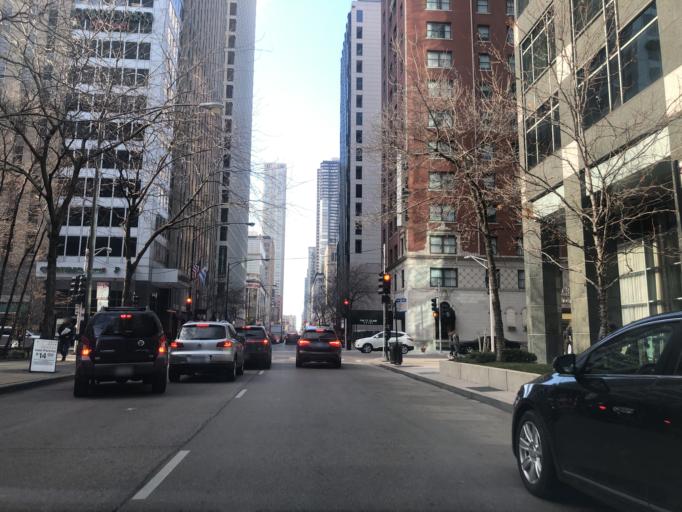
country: US
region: Illinois
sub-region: Cook County
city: Chicago
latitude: 41.8933
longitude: -87.6222
